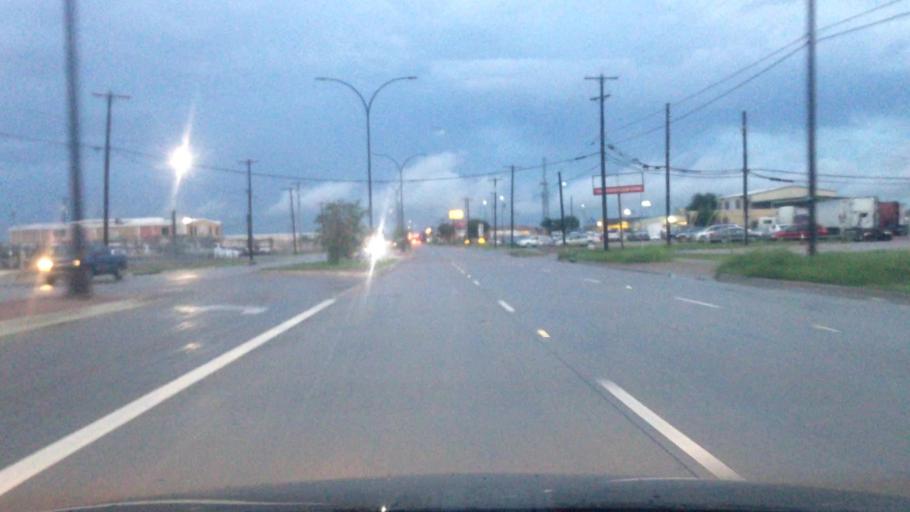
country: US
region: Texas
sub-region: Tarrant County
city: Arlington
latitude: 32.7368
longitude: -97.0548
